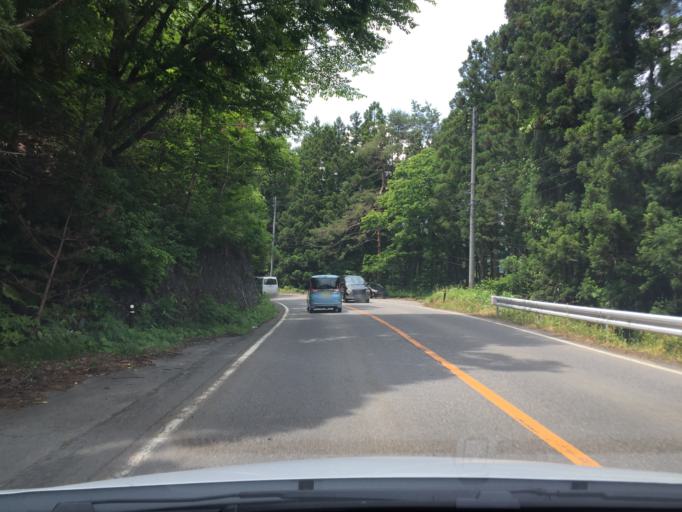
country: JP
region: Fukushima
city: Inawashiro
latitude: 37.6185
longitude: 140.1162
